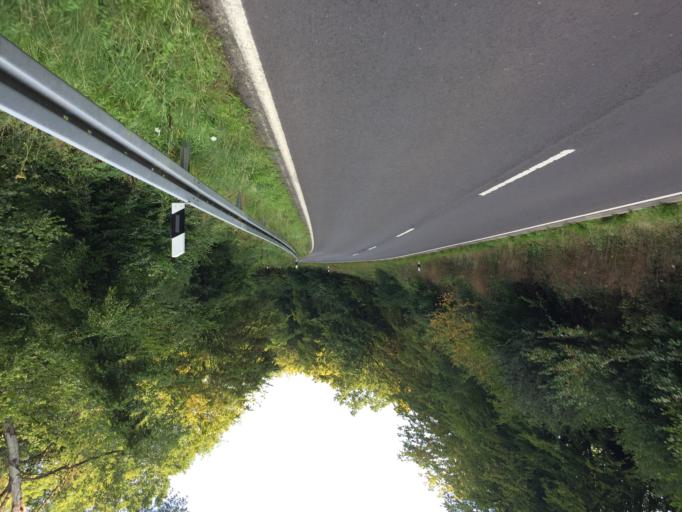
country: DE
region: Hesse
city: Lollar
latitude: 50.6519
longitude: 8.6868
